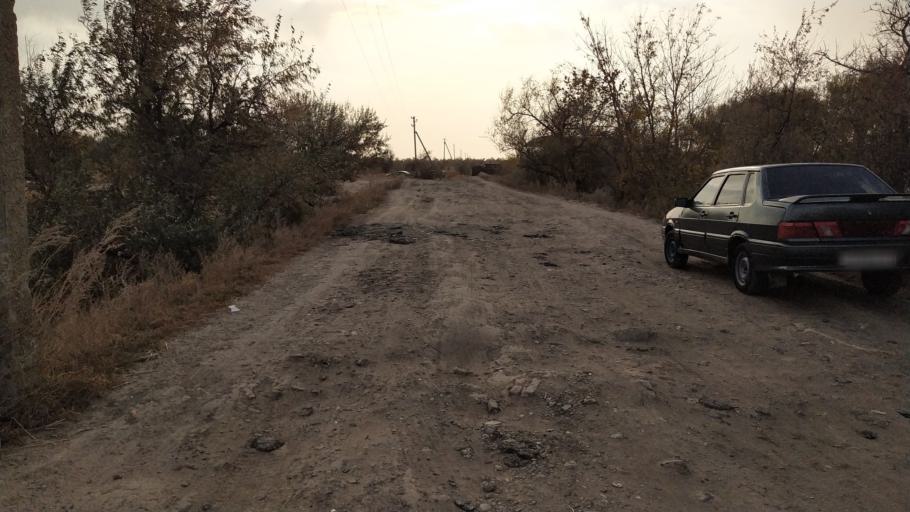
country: RU
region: Rostov
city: Kuleshovka
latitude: 47.1419
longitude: 39.5791
